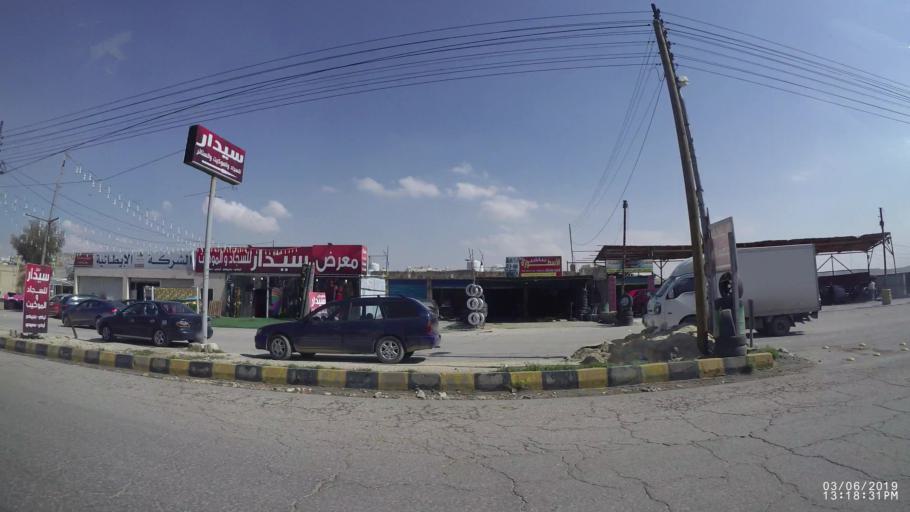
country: JO
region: Zarqa
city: Zarqa
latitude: 32.0368
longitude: 36.0920
